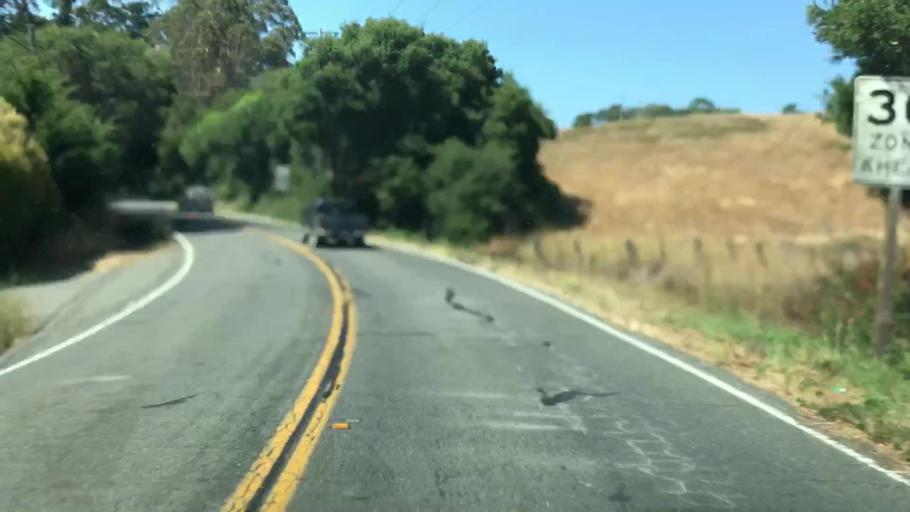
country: US
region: California
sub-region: Marin County
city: Lagunitas-Forest Knolls
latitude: 38.0385
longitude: -122.7842
